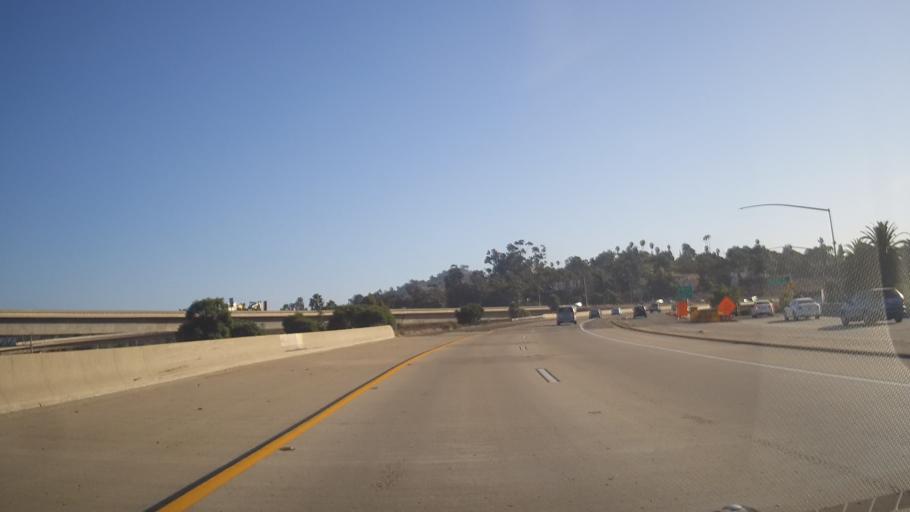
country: US
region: California
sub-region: San Diego County
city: Spring Valley
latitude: 32.7528
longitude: -117.0112
